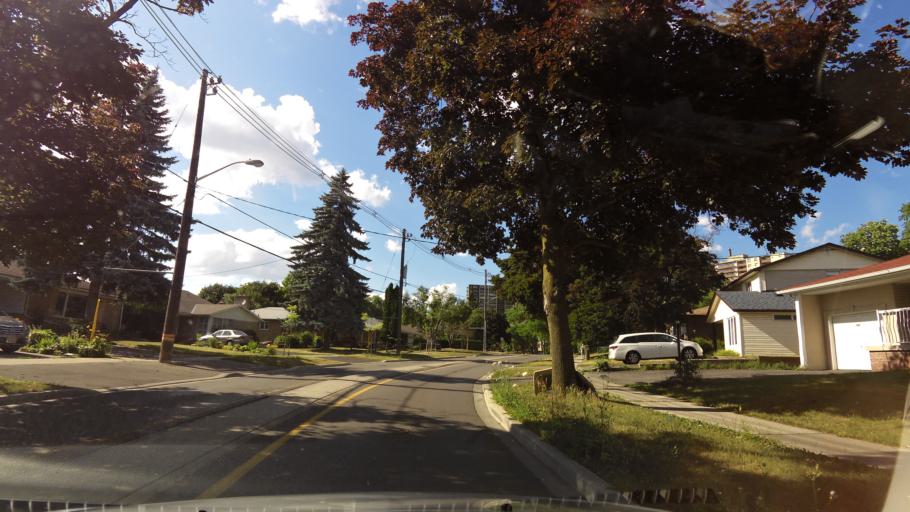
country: CA
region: Ontario
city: Willowdale
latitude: 43.7787
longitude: -79.3538
